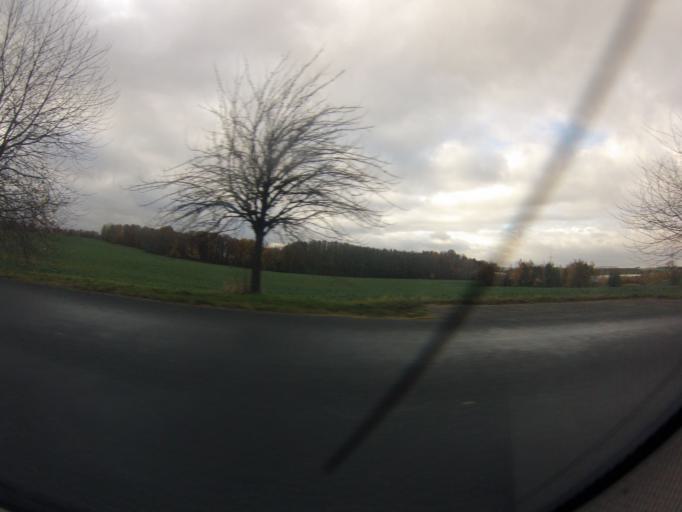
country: DE
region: Thuringia
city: Heyersdorf
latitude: 50.8460
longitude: 12.3315
